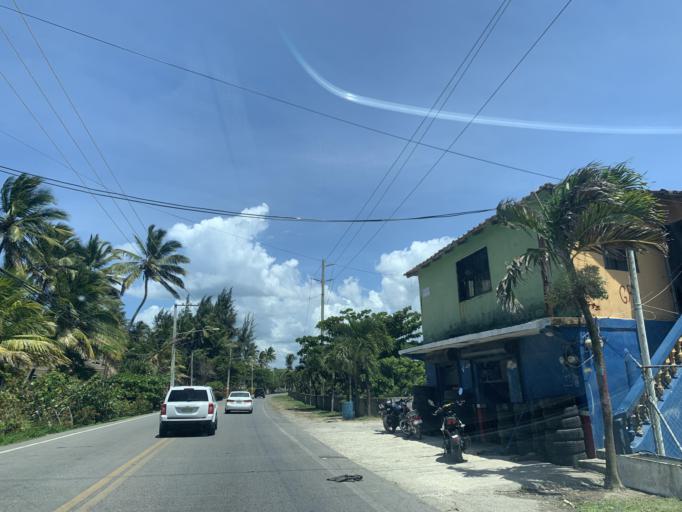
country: DO
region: Puerto Plata
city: Cabarete
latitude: 19.7463
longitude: -70.3957
